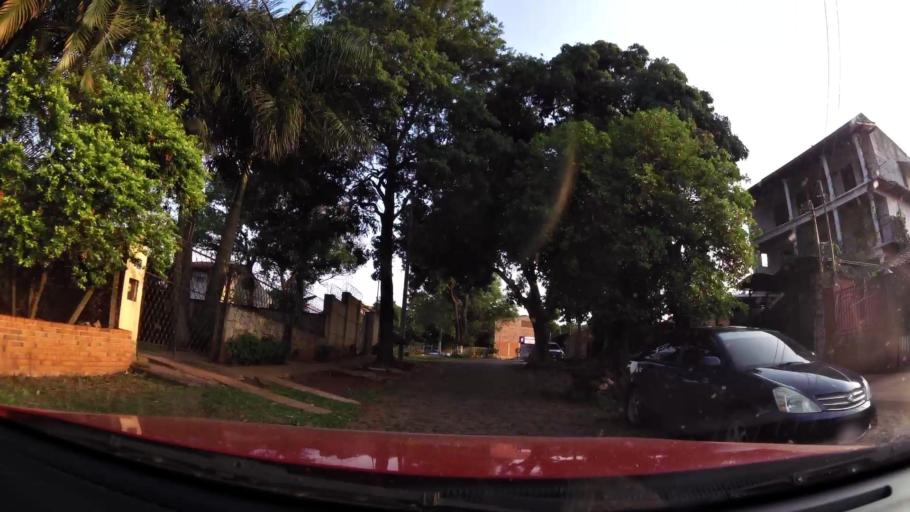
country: PY
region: Central
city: Lambare
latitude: -25.3534
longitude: -57.6012
